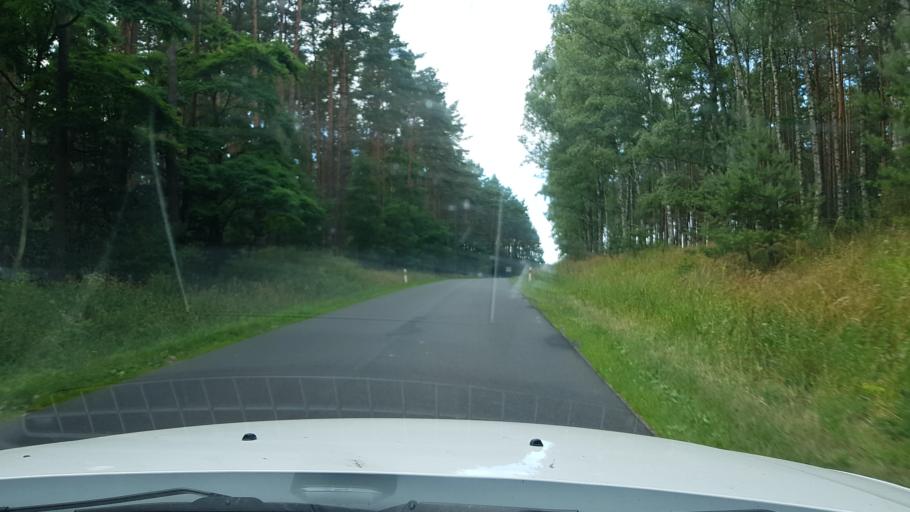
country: PL
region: West Pomeranian Voivodeship
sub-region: Powiat drawski
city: Zlocieniec
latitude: 53.5165
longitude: 16.0207
